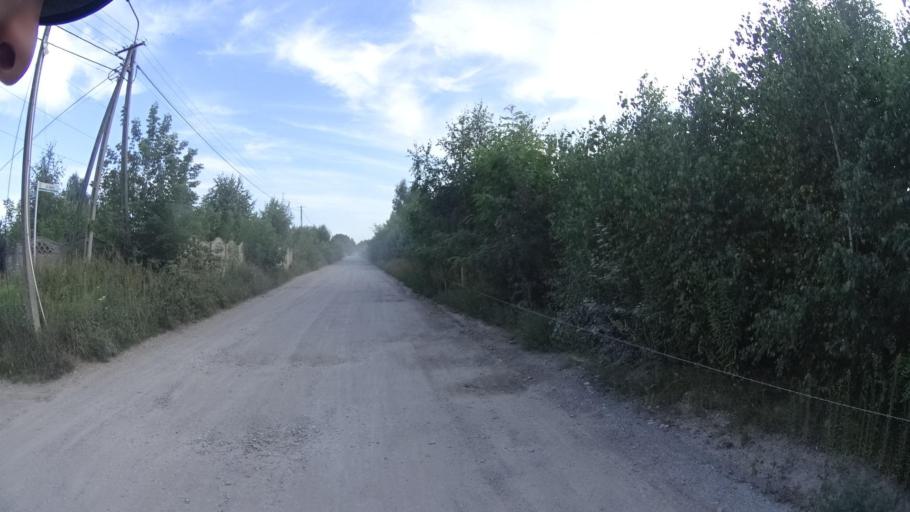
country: PL
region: Masovian Voivodeship
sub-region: Powiat piaseczynski
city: Tarczyn
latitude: 51.9751
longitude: 20.8537
